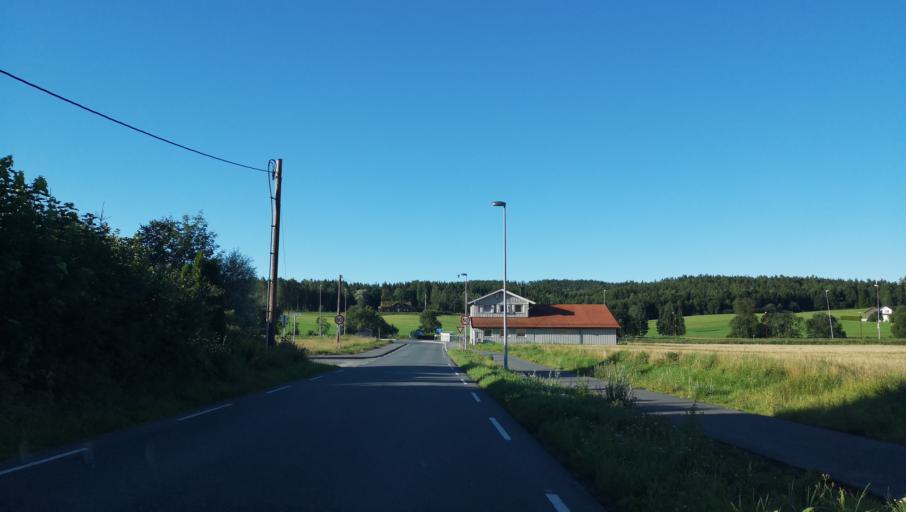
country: NO
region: Ostfold
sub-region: Hobol
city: Knappstad
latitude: 59.6215
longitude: 11.0236
